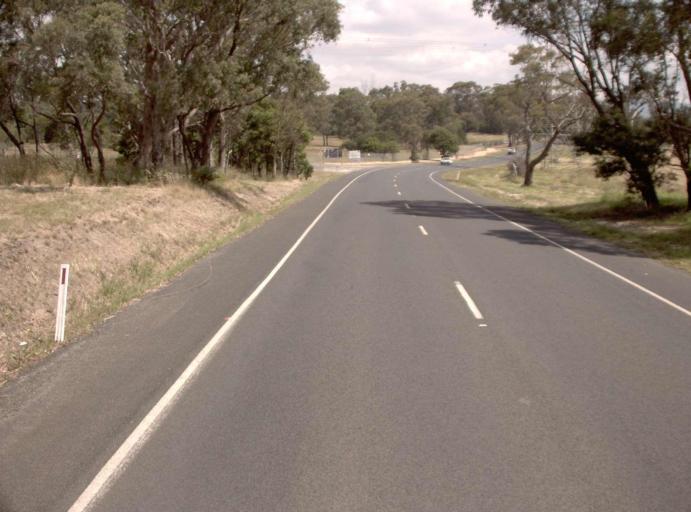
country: AU
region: Victoria
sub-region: Latrobe
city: Traralgon
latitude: -38.2535
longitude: 146.5502
